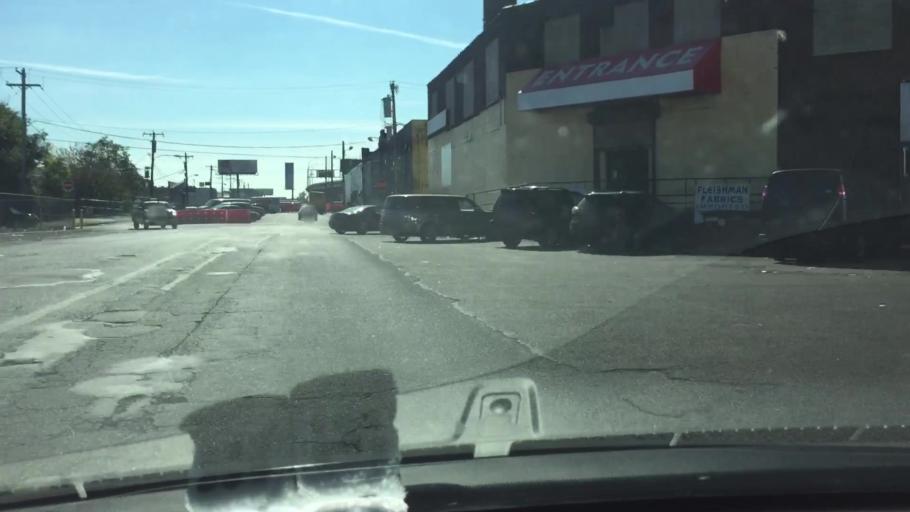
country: US
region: New Jersey
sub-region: Camden County
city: Camden
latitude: 39.9195
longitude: -75.1467
